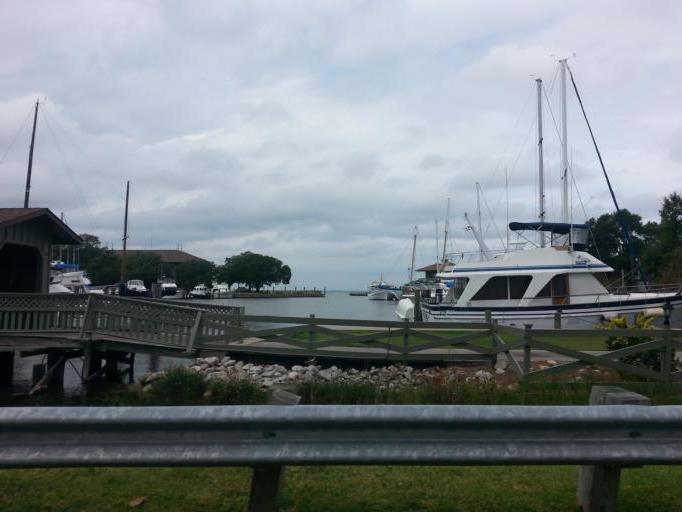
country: US
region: Alabama
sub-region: Baldwin County
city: Point Clear
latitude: 30.4859
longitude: -87.9323
